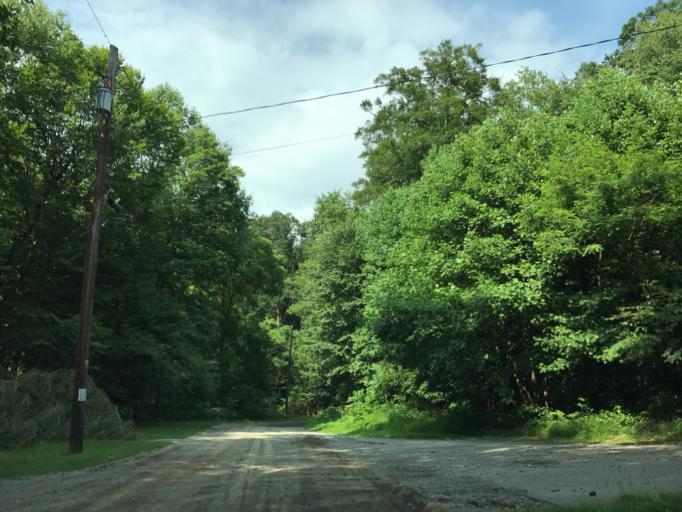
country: US
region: Pennsylvania
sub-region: Lancaster County
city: Quarryville
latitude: 39.7653
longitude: -76.2197
